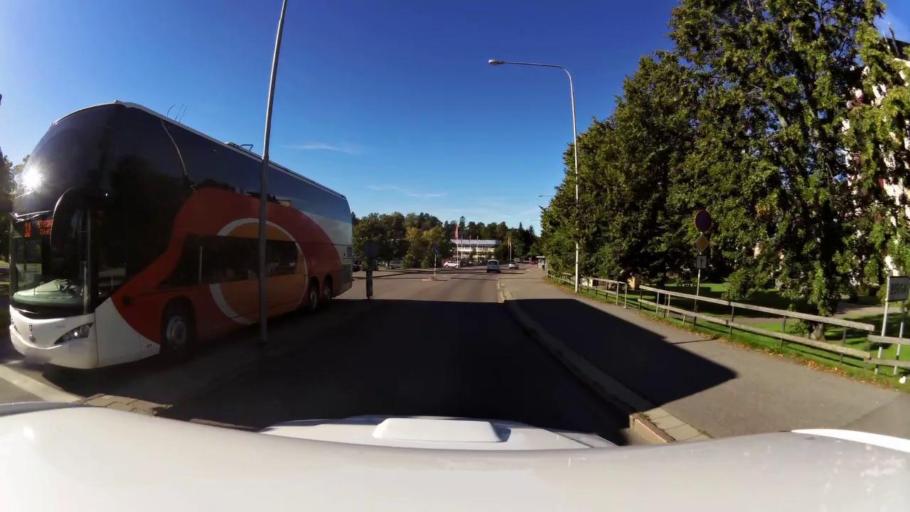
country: SE
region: OEstergoetland
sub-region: Linkopings Kommun
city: Linkoping
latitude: 58.4150
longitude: 15.6551
